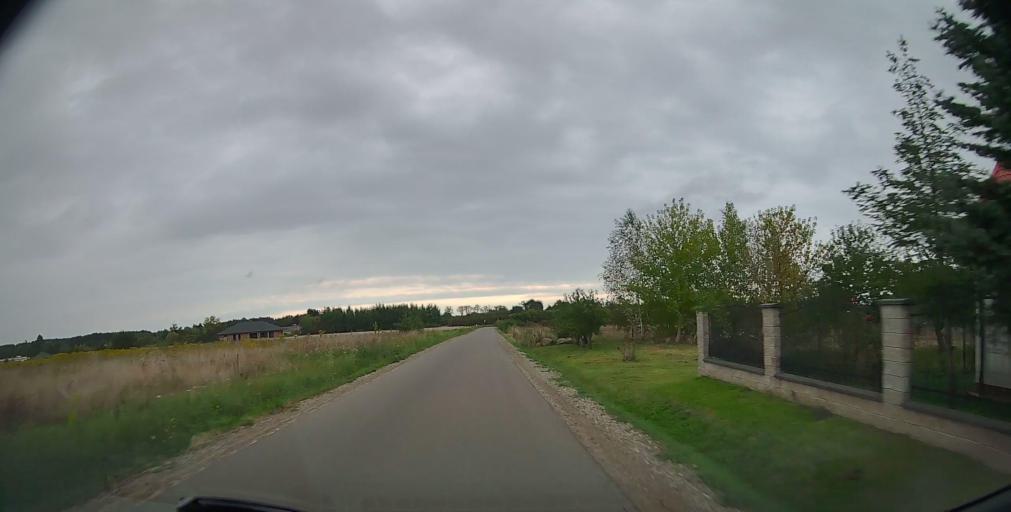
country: PL
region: Masovian Voivodeship
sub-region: Powiat radomski
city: Jedlinsk
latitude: 51.4524
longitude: 21.1017
